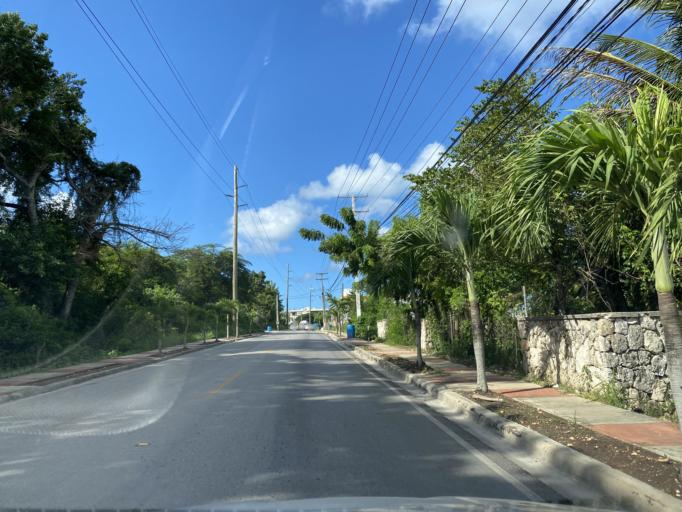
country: DO
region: La Romana
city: La Romana
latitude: 18.3707
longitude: -68.8327
